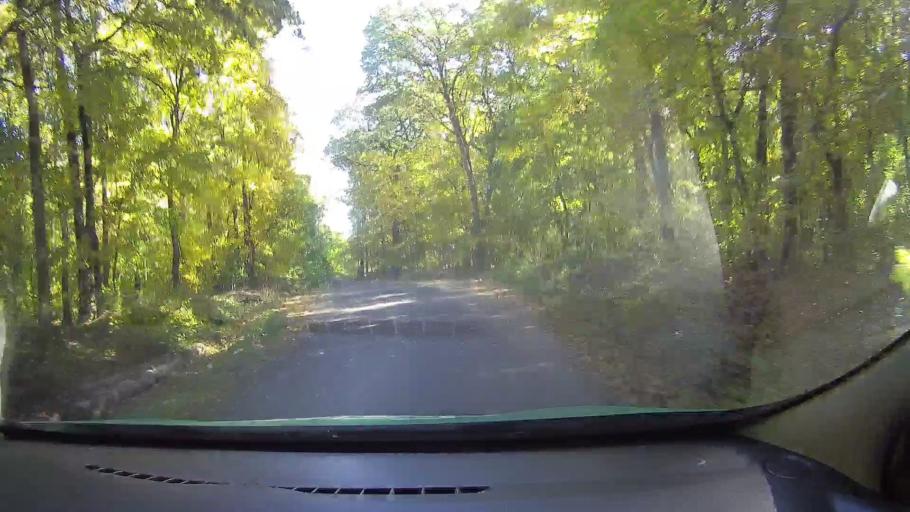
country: RO
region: Satu Mare
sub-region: Comuna Doba
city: Doba
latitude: 47.7139
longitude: 22.7478
